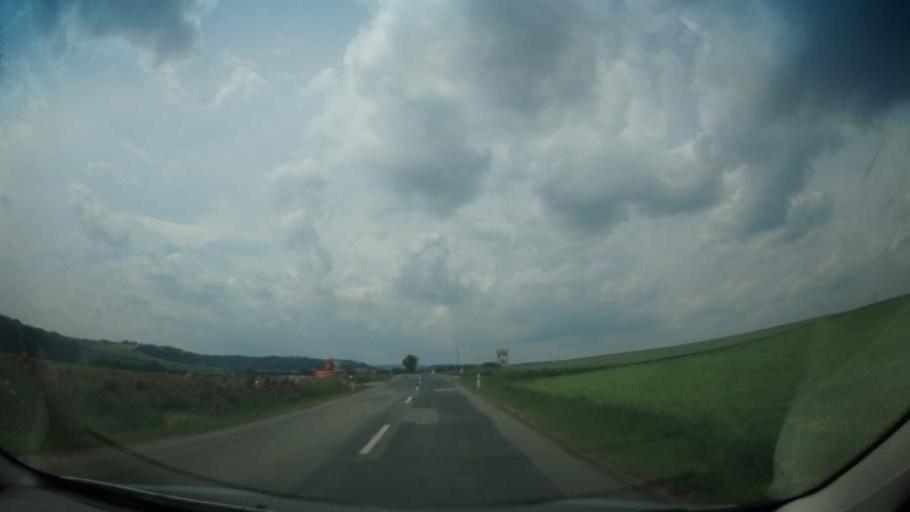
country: CZ
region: South Moravian
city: Boritov
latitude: 49.4348
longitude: 16.5692
